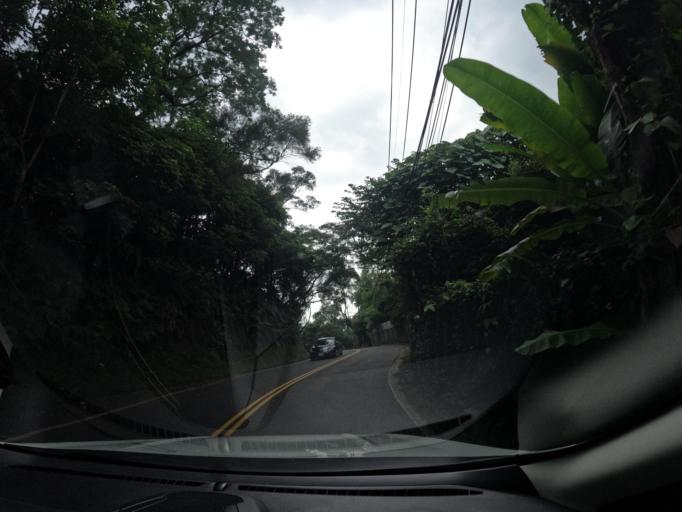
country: TW
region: Taiwan
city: Daxi
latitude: 24.9055
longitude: 121.3986
